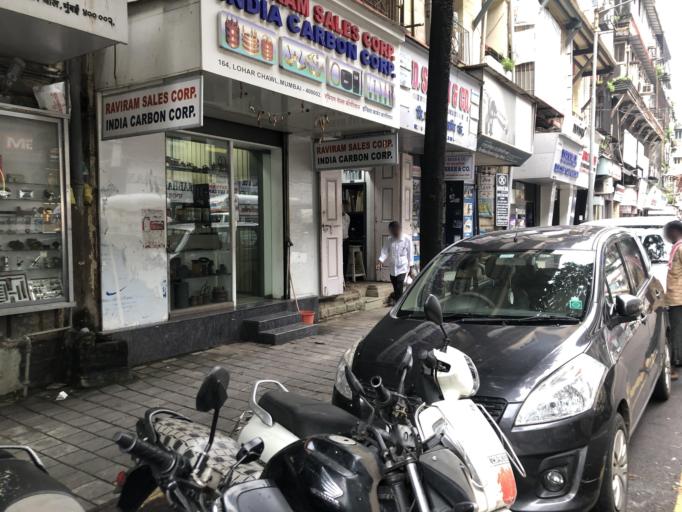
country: IN
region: Maharashtra
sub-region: Raigarh
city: Uran
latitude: 18.9465
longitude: 72.8304
